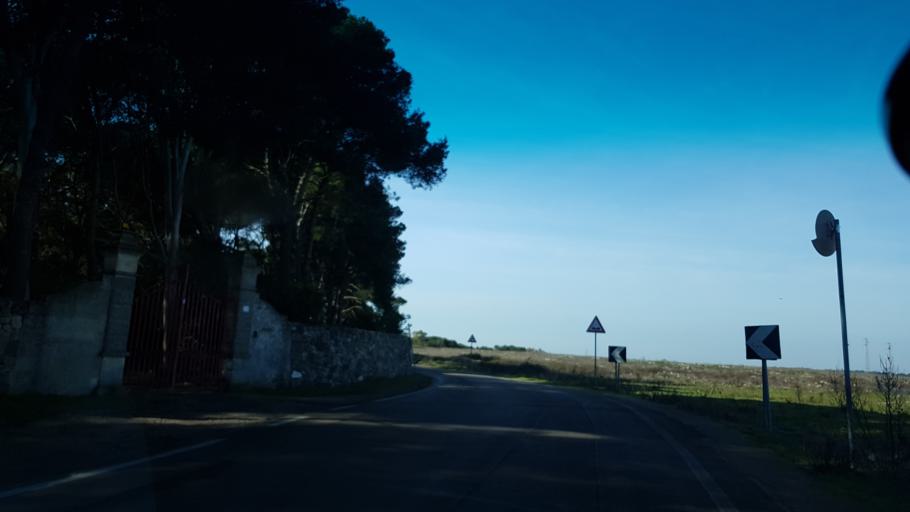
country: IT
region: Apulia
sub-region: Provincia di Lecce
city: Lecce
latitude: 40.3493
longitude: 18.1375
